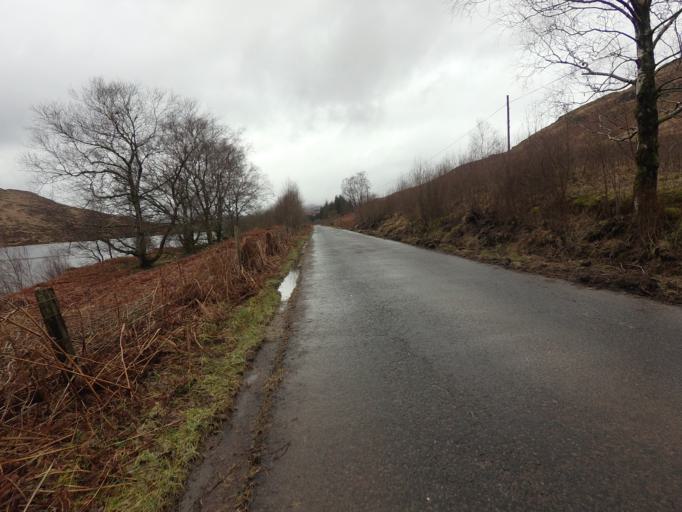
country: GB
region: Scotland
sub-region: Argyll and Bute
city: Garelochhead
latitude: 56.2484
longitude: -4.6381
